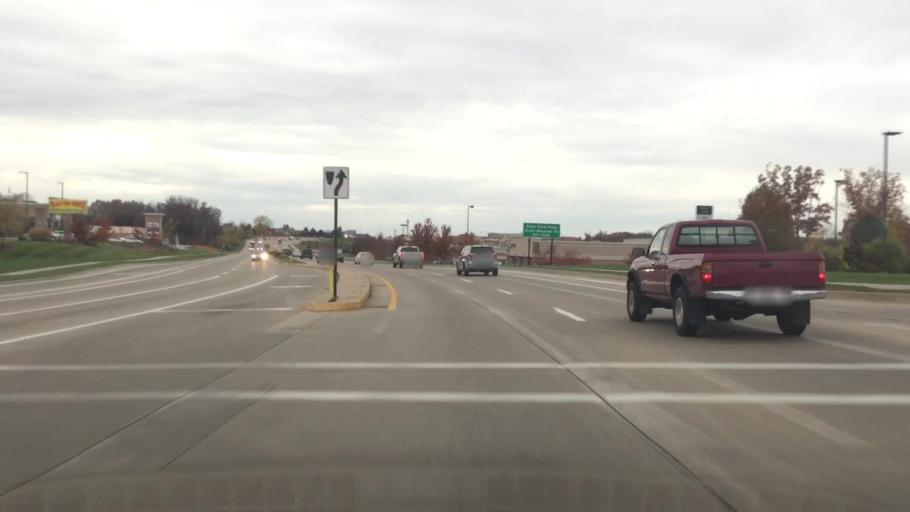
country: US
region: Missouri
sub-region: Boone County
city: Columbia
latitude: 38.9133
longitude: -92.3190
